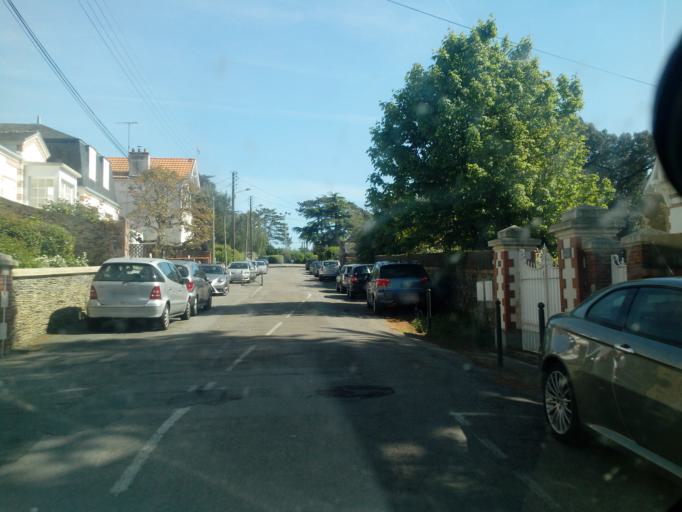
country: FR
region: Pays de la Loire
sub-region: Departement de la Loire-Atlantique
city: Pornic
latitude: 47.1115
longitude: -2.1034
